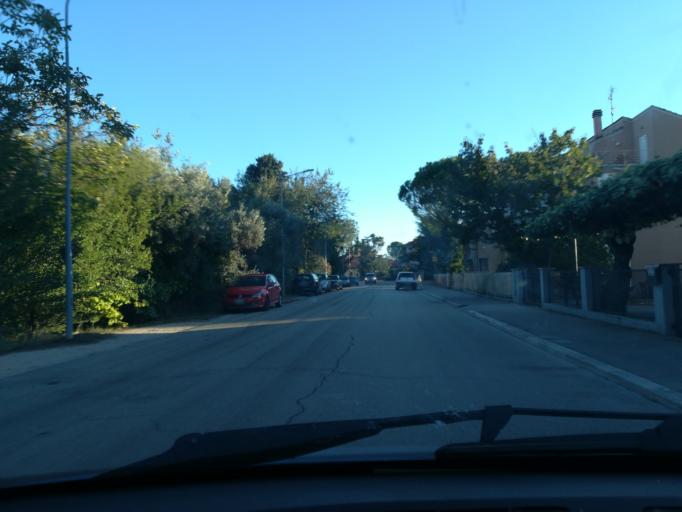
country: IT
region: The Marches
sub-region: Provincia di Macerata
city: Piediripa
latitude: 43.2773
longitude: 13.4841
